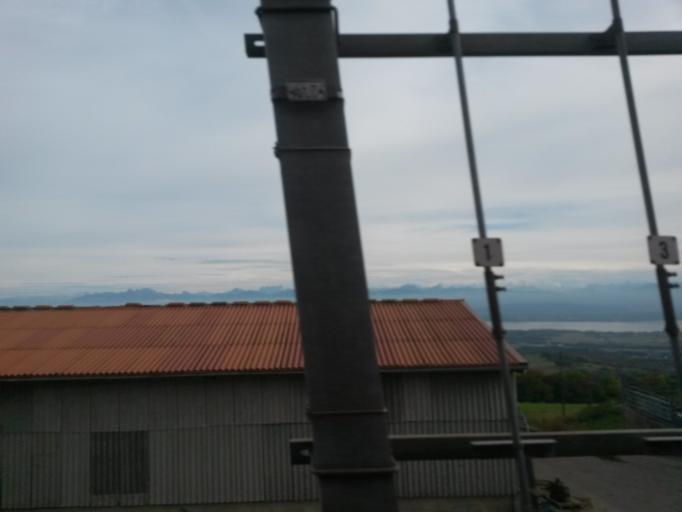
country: CH
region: Vaud
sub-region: Nyon District
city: Arzier
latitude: 46.4585
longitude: 6.2115
